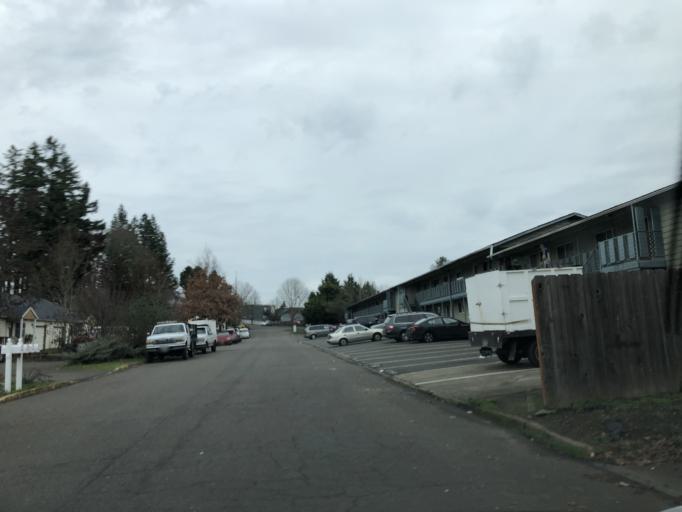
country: US
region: Oregon
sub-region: Washington County
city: Tigard
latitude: 45.4297
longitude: -122.7671
